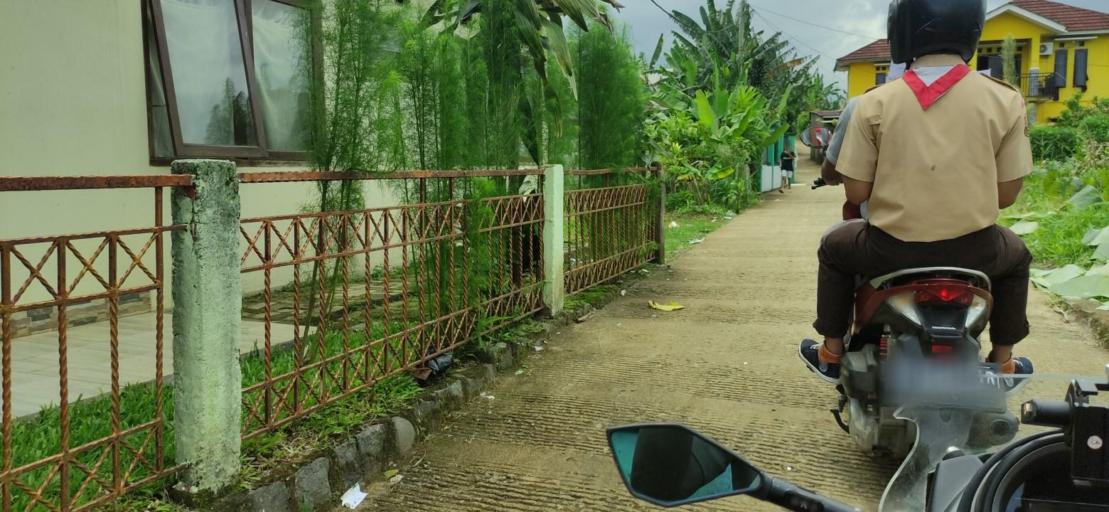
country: ID
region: West Java
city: Caringin
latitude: -6.6458
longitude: 106.8866
